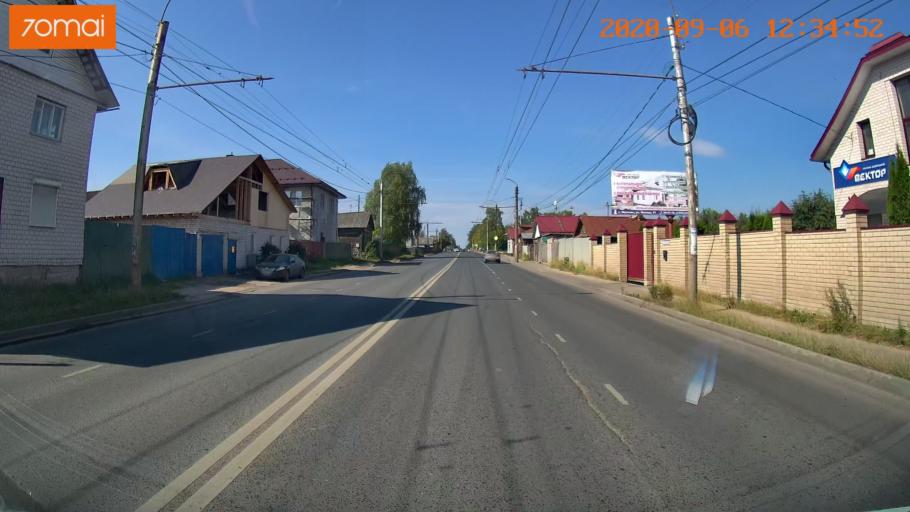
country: RU
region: Ivanovo
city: Bogorodskoye
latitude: 57.0175
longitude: 41.0000
